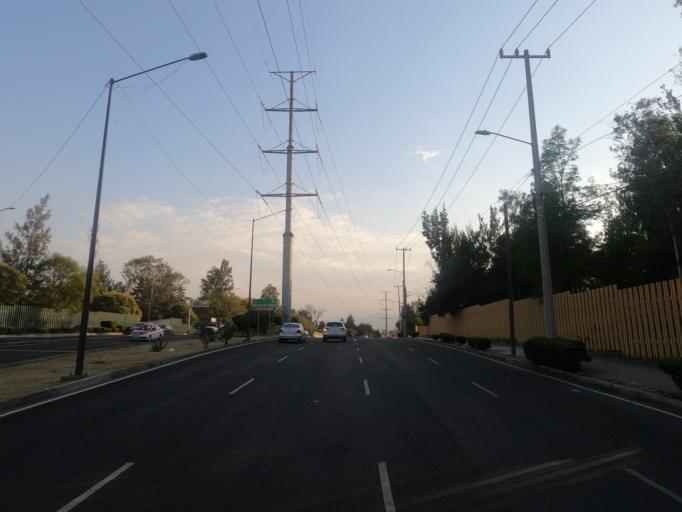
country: MX
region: Mexico City
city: Alvaro Obregon
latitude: 19.3536
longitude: -99.2069
